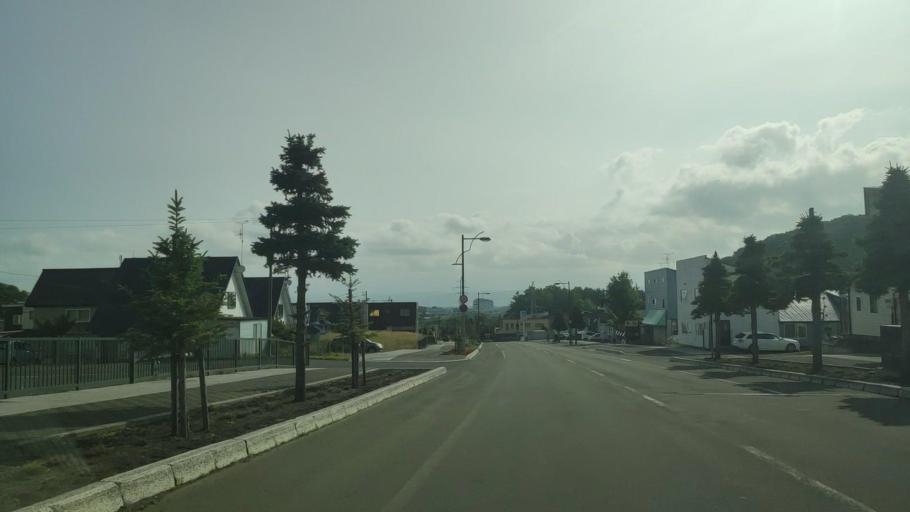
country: JP
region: Hokkaido
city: Shimo-furano
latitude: 43.3436
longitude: 142.3684
